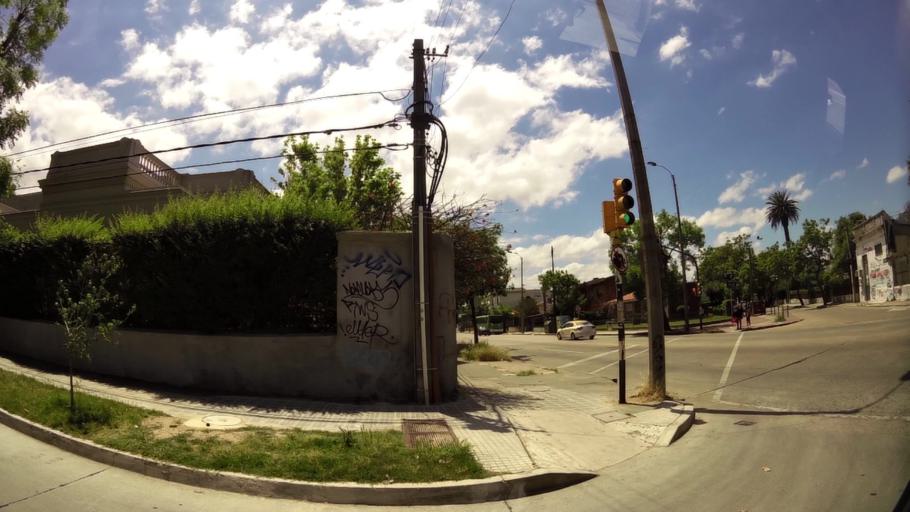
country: UY
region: Montevideo
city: Montevideo
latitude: -34.8643
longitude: -56.1930
